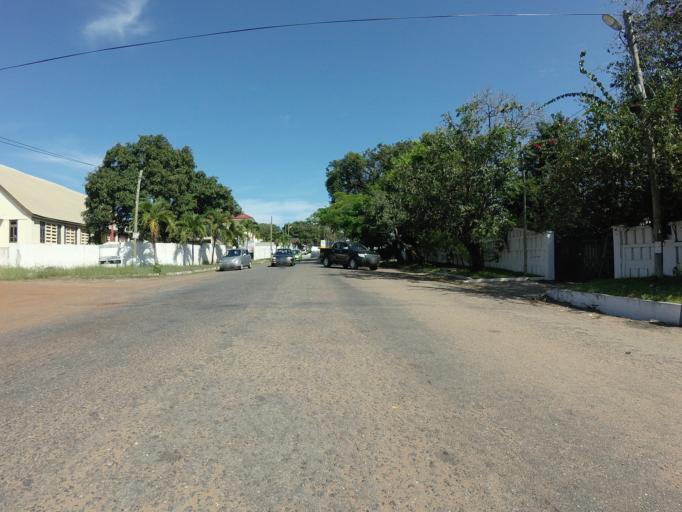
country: GH
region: Greater Accra
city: Accra
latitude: 5.5724
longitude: -0.1704
